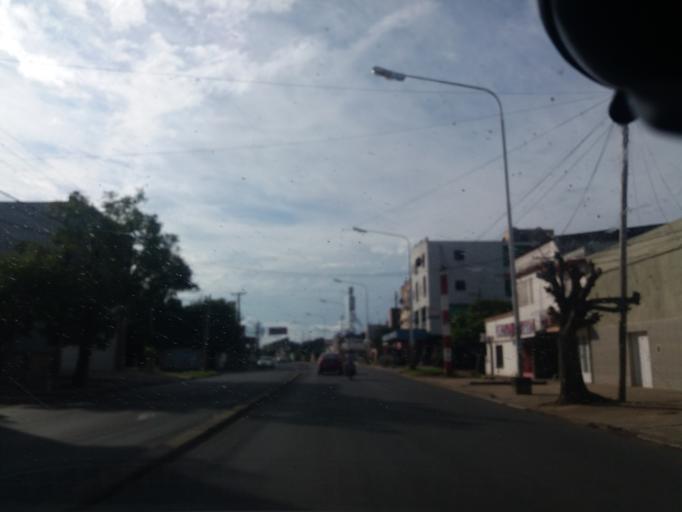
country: AR
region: Corrientes
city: Corrientes
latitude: -27.4904
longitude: -58.8202
